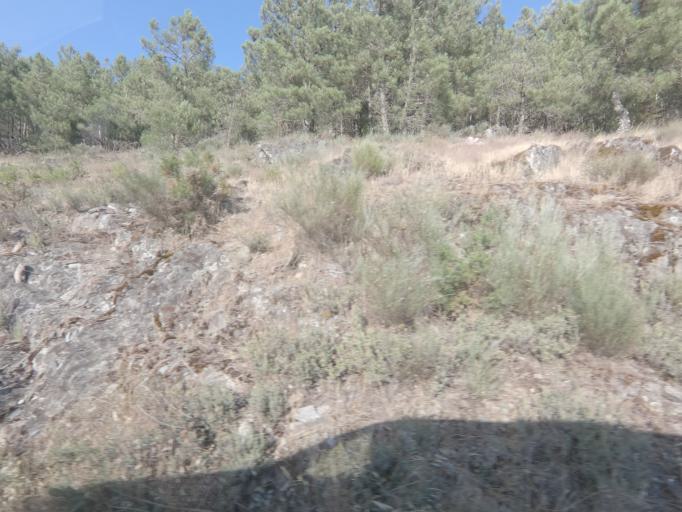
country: PT
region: Vila Real
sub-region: Sabrosa
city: Vilela
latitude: 41.1915
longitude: -7.6188
